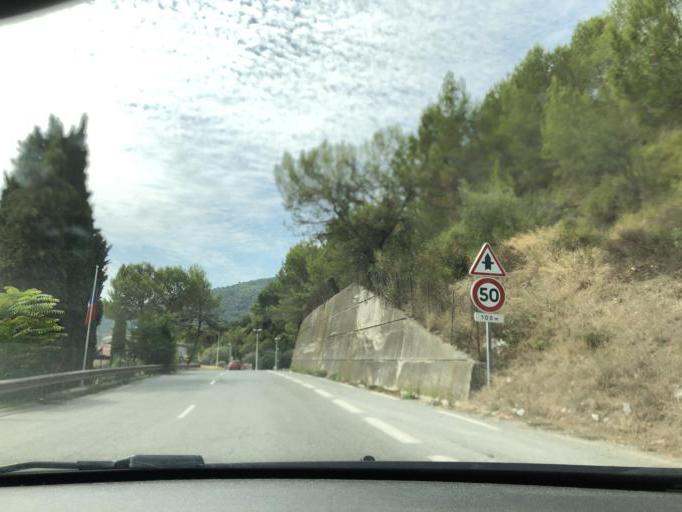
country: FR
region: Provence-Alpes-Cote d'Azur
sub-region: Departement des Alpes-Maritimes
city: La Trinite
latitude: 43.7441
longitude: 7.3093
